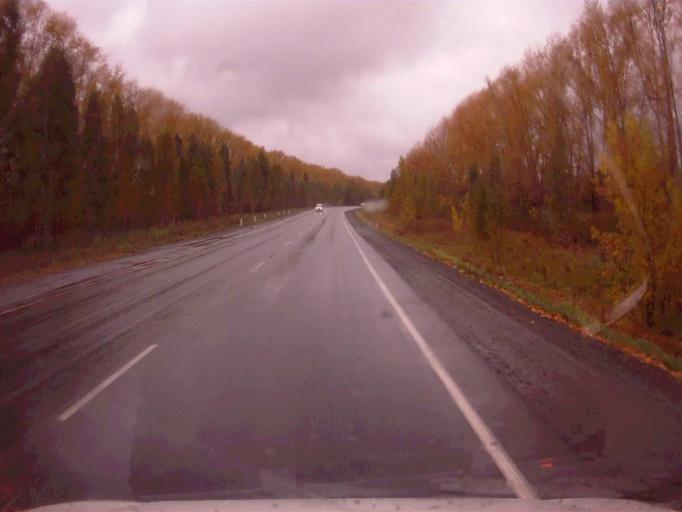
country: RU
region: Chelyabinsk
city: Argayash
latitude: 55.4500
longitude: 60.9391
